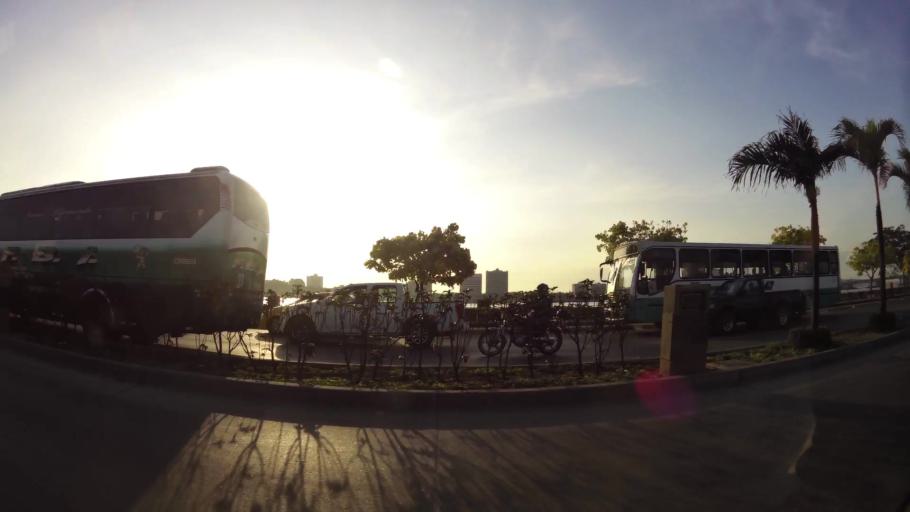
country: EC
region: Guayas
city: Eloy Alfaro
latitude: -2.1472
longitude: -79.8765
